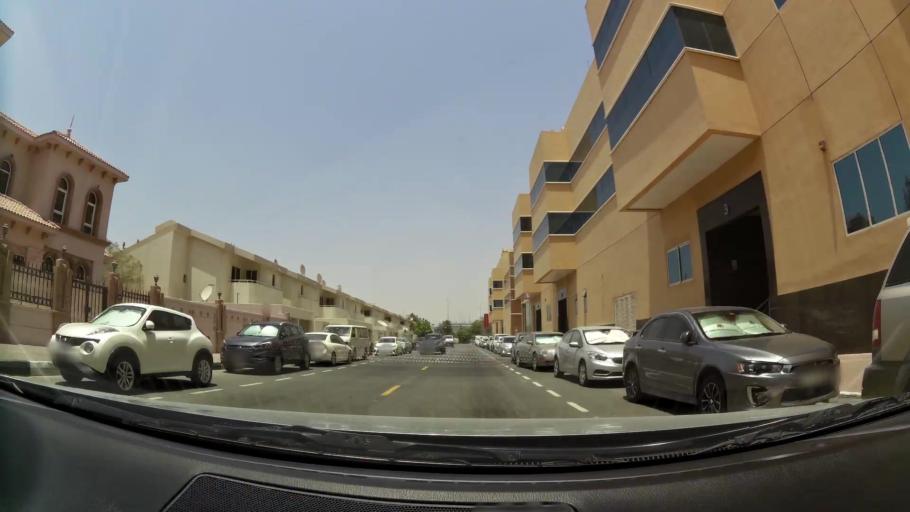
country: AE
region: Dubai
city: Dubai
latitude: 25.1786
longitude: 55.2463
